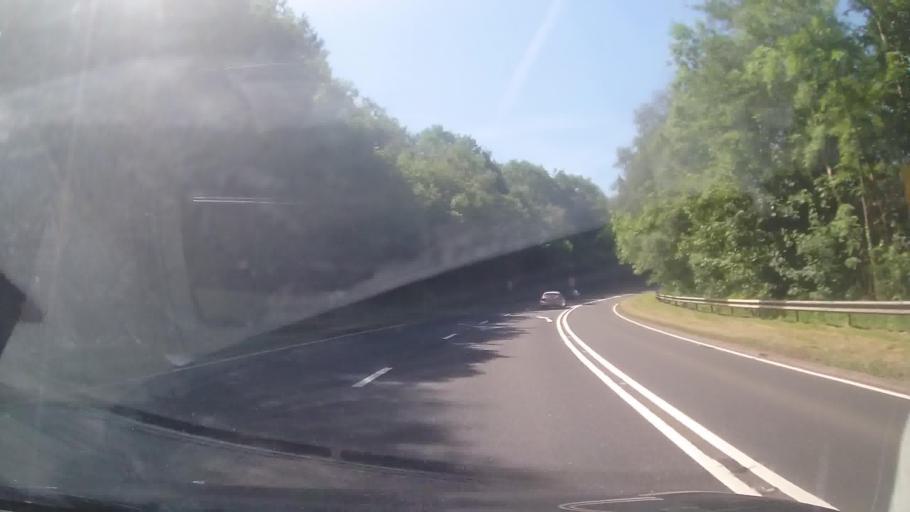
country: GB
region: England
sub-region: Herefordshire
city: Hope under Dinmore
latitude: 52.1637
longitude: -2.7186
